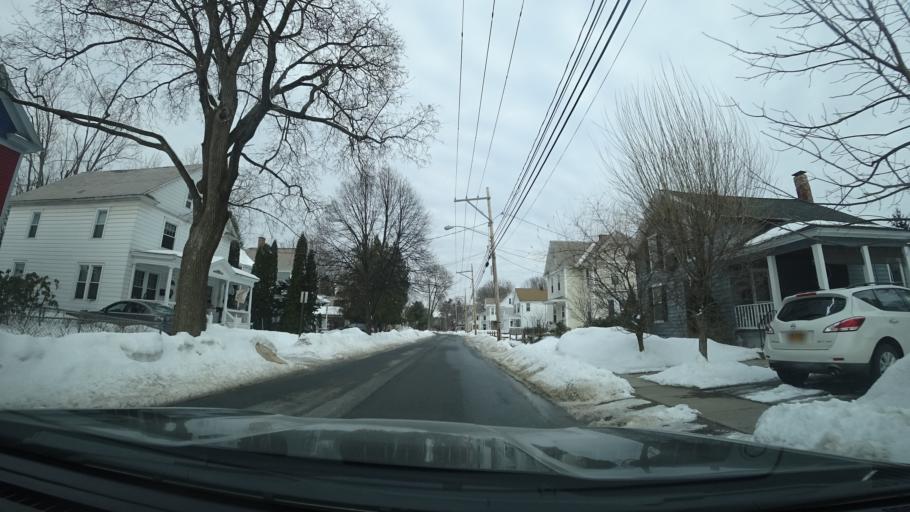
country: US
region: New York
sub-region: Warren County
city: Glens Falls
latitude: 43.3119
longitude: -73.6550
